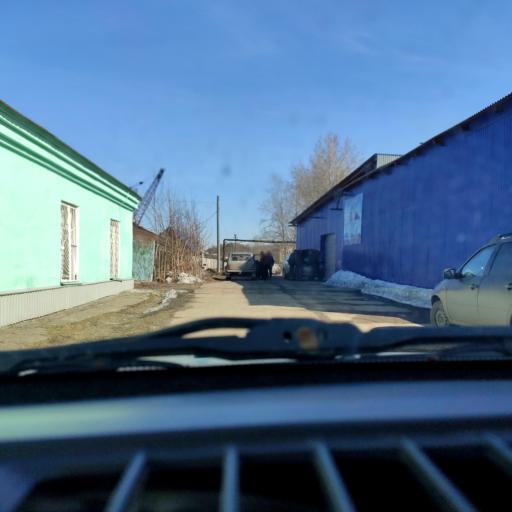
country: RU
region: Perm
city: Perm
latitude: 58.0774
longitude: 56.3454
